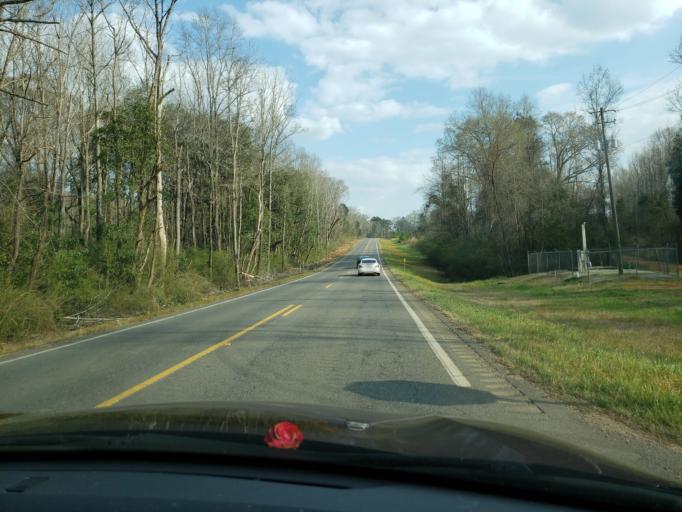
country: US
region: Alabama
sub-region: Hale County
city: Greensboro
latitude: 32.7114
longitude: -87.6126
